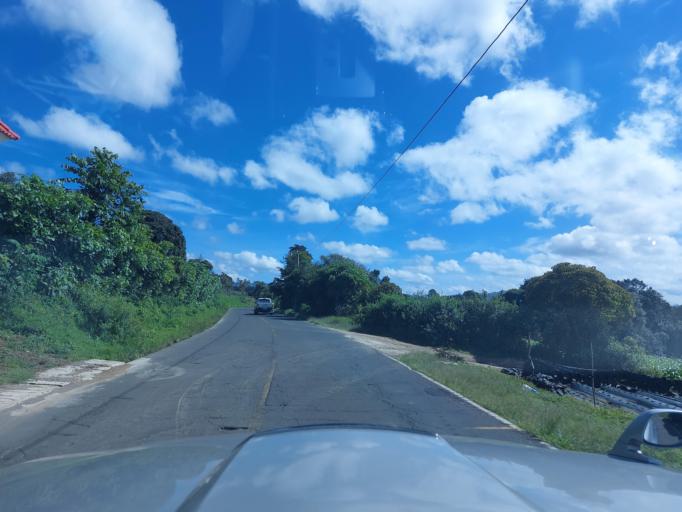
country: GT
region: Chimaltenango
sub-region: Municipio de Zaragoza
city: Zaragoza
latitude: 14.6573
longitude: -90.8971
